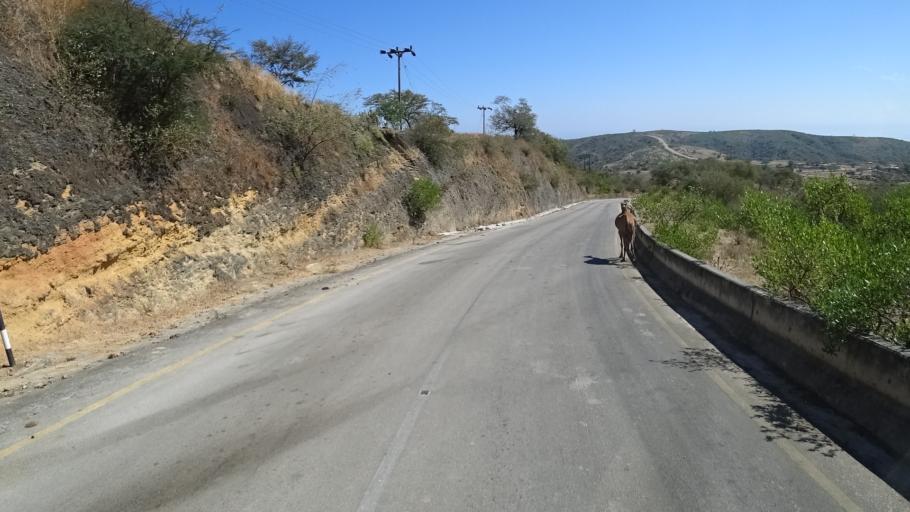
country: YE
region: Al Mahrah
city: Hawf
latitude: 16.7626
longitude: 53.3387
